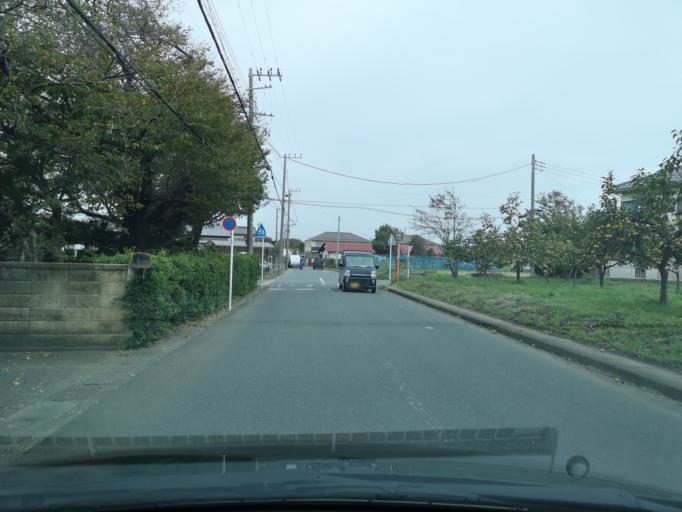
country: JP
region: Kanagawa
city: Chigasaki
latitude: 35.3887
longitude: 139.4013
